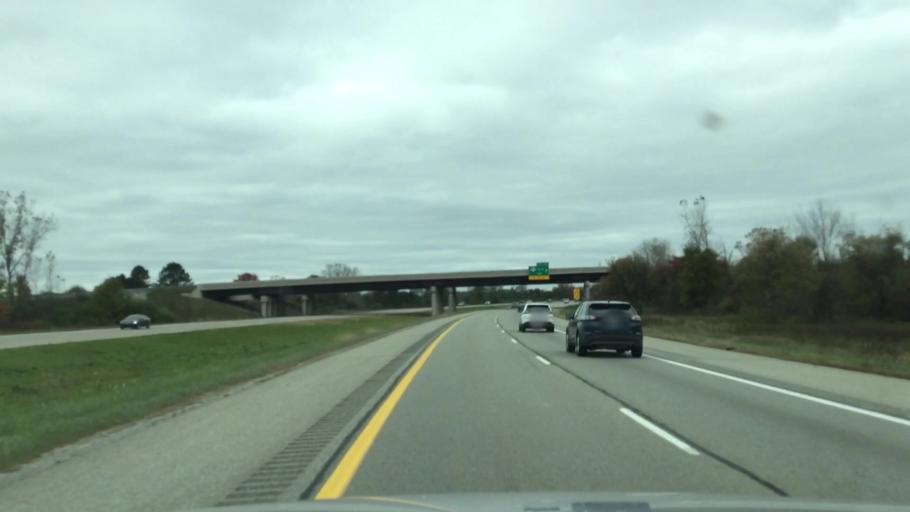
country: US
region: Michigan
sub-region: Washtenaw County
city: Ypsilanti
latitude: 42.3279
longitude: -83.6299
